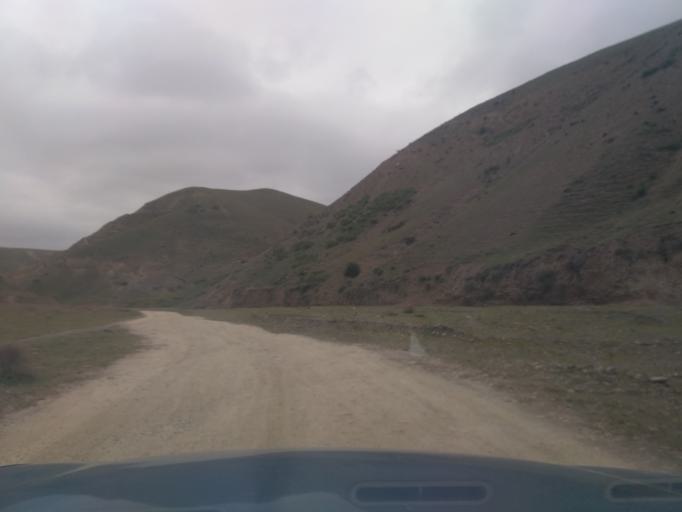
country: UZ
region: Jizzax
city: Zomin
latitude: 39.8485
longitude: 68.3968
